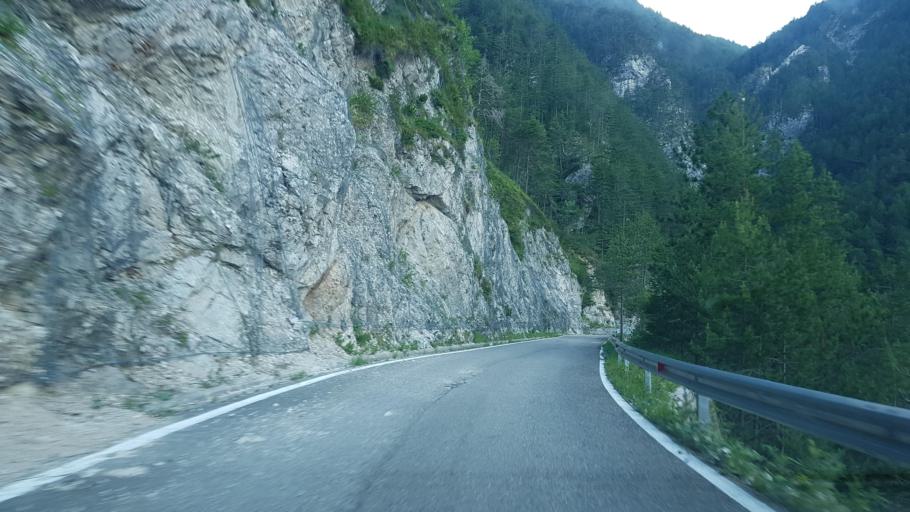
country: IT
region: Friuli Venezia Giulia
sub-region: Provincia di Udine
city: Dogna
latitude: 46.4573
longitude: 13.3767
